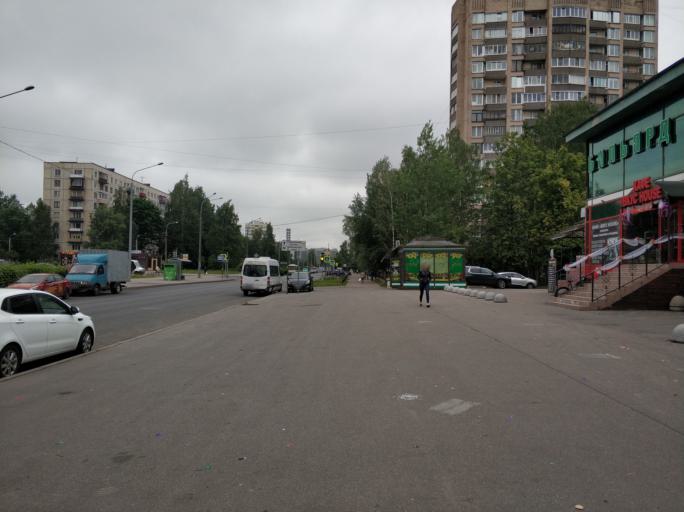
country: RU
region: St.-Petersburg
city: Grazhdanka
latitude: 60.0409
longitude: 30.4146
